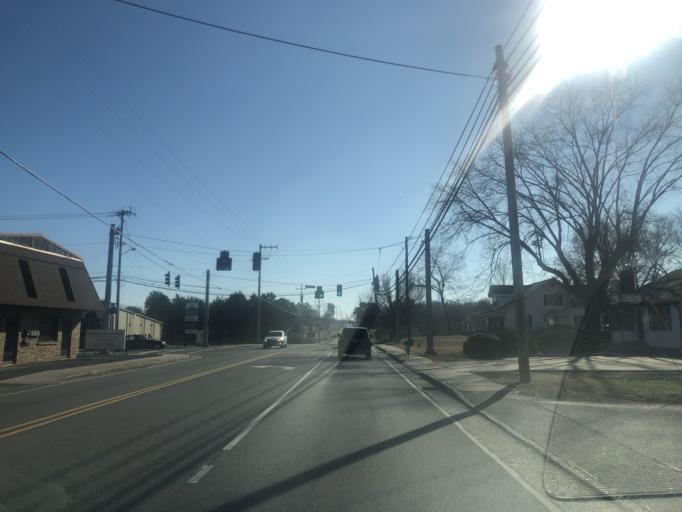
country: US
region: Tennessee
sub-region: Rutherford County
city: La Vergne
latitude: 36.0146
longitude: -86.5750
